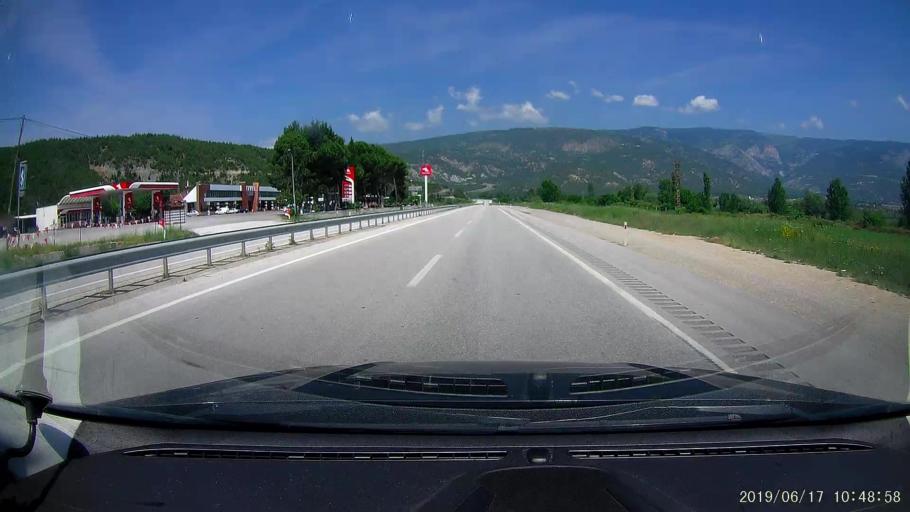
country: TR
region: Corum
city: Hacihamza
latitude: 41.0955
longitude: 34.4199
